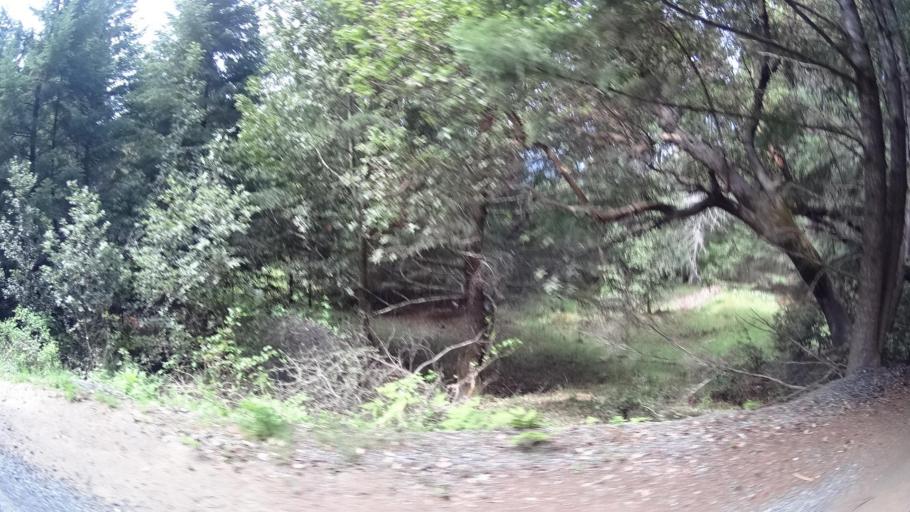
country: US
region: California
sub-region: Humboldt County
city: Redway
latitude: 40.0372
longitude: -123.8405
